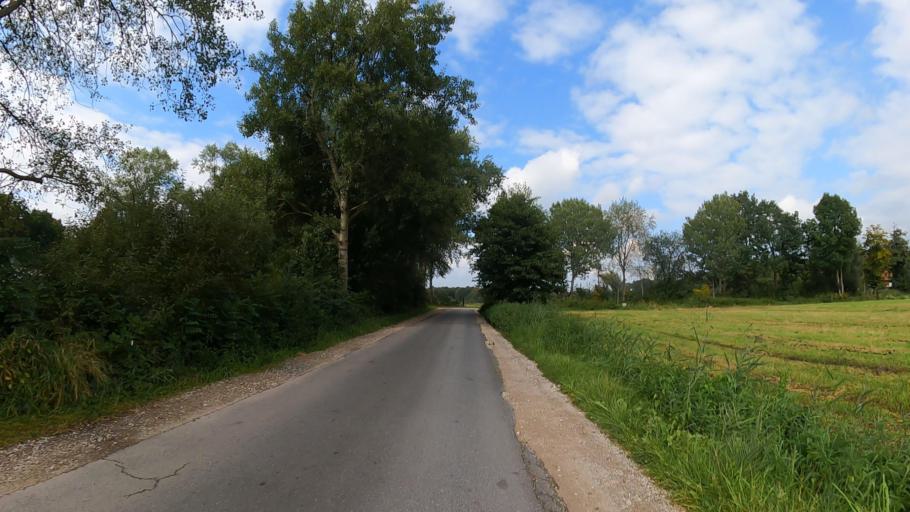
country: DE
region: Schleswig-Holstein
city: Tornesch
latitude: 53.7192
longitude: 9.7039
